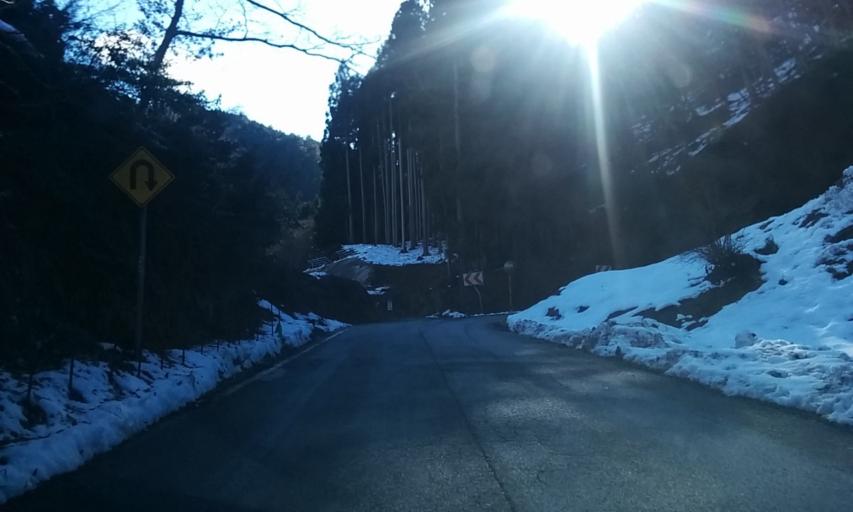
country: JP
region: Hyogo
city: Toyooka
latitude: 35.4124
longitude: 134.9562
